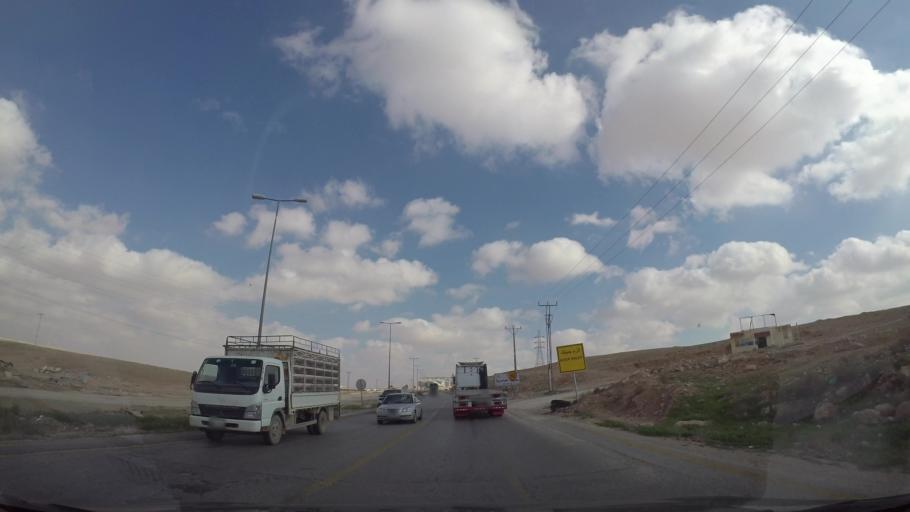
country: JO
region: Amman
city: Al Jizah
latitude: 31.6283
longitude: 35.9882
